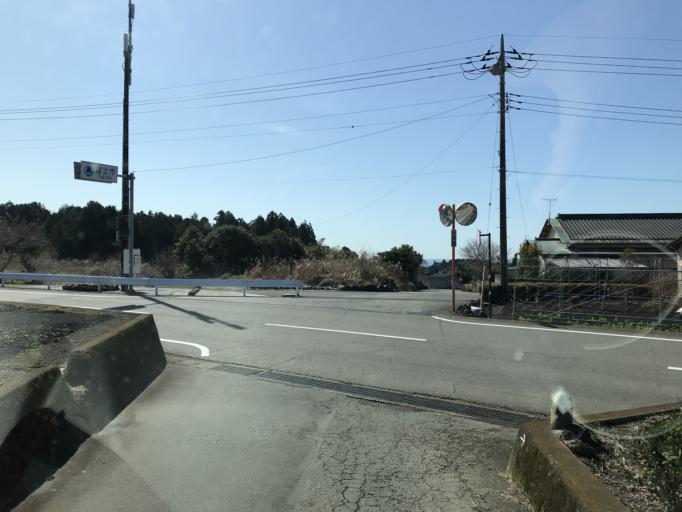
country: JP
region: Shizuoka
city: Fujinomiya
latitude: 35.2402
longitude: 138.6593
